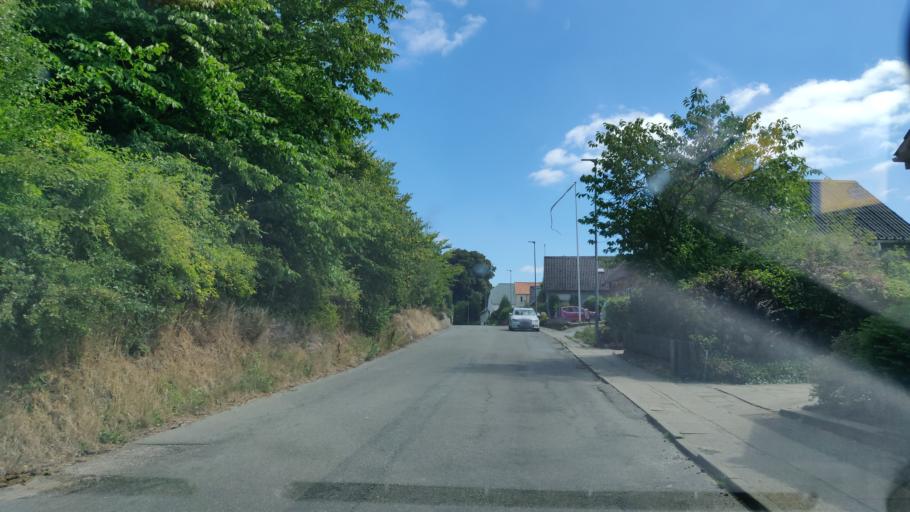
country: DK
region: South Denmark
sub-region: Kolding Kommune
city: Kolding
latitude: 55.5271
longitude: 9.5396
